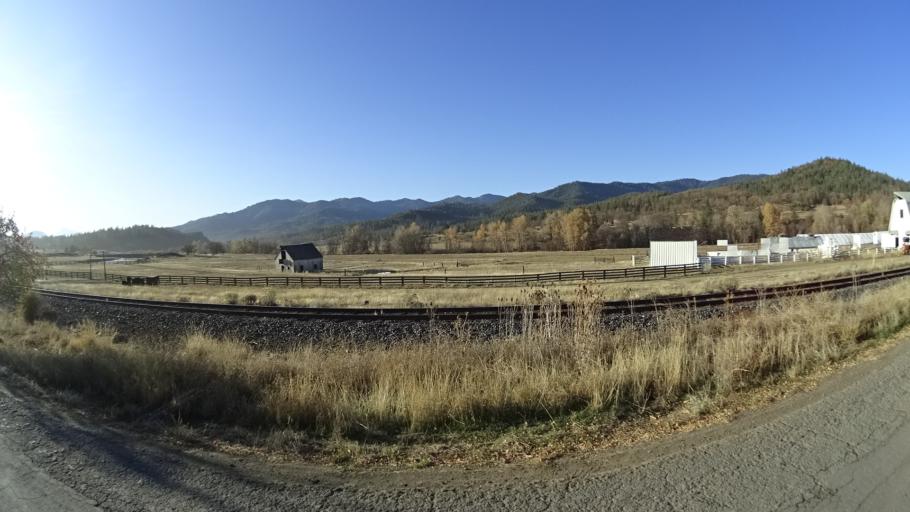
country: US
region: Oregon
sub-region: Jackson County
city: Ashland
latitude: 42.0018
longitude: -122.6397
